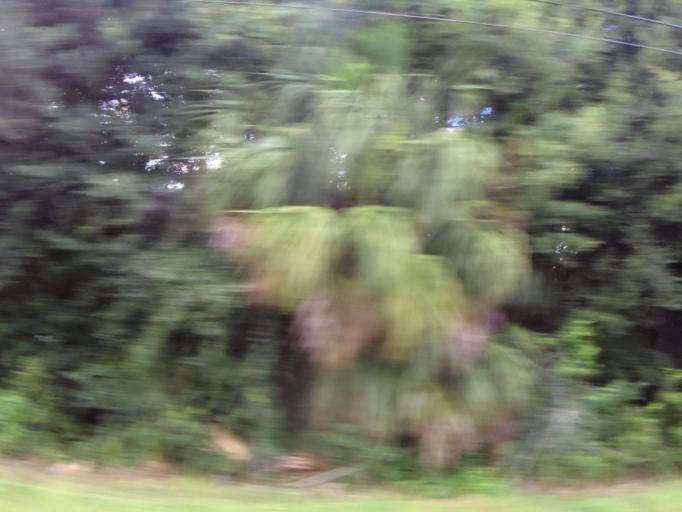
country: US
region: Florida
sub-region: Duval County
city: Jacksonville
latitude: 30.3202
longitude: -81.7573
